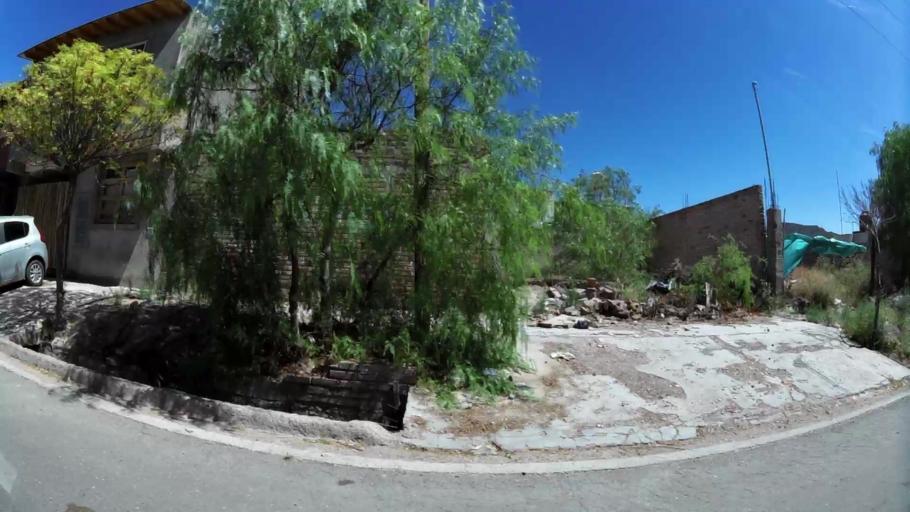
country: AR
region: Mendoza
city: Las Heras
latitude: -32.8391
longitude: -68.8721
